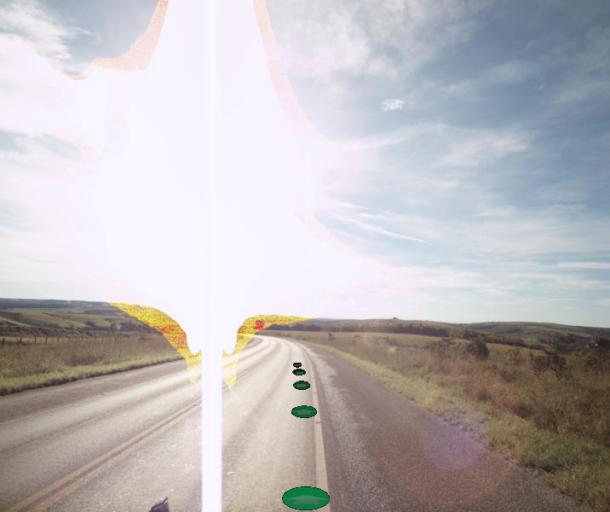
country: BR
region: Goias
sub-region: Abadiania
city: Abadiania
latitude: -15.7858
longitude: -48.4798
